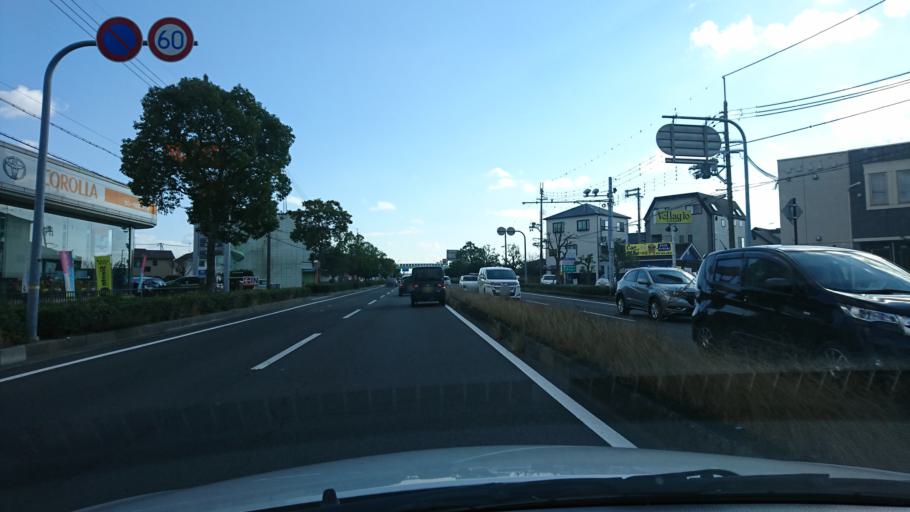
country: JP
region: Hyogo
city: Kakogawacho-honmachi
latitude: 34.7156
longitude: 134.8772
